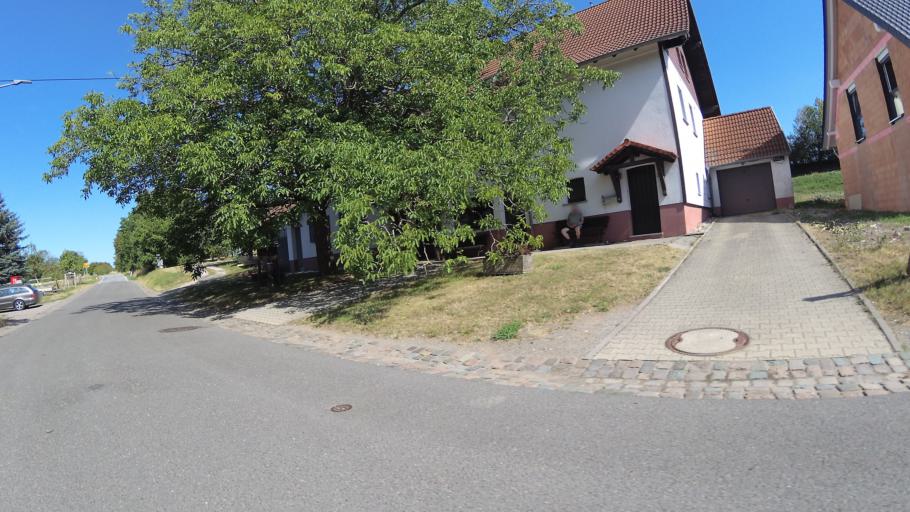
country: DE
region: Rheinland-Pfalz
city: Hornbach
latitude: 49.1400
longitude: 7.3100
